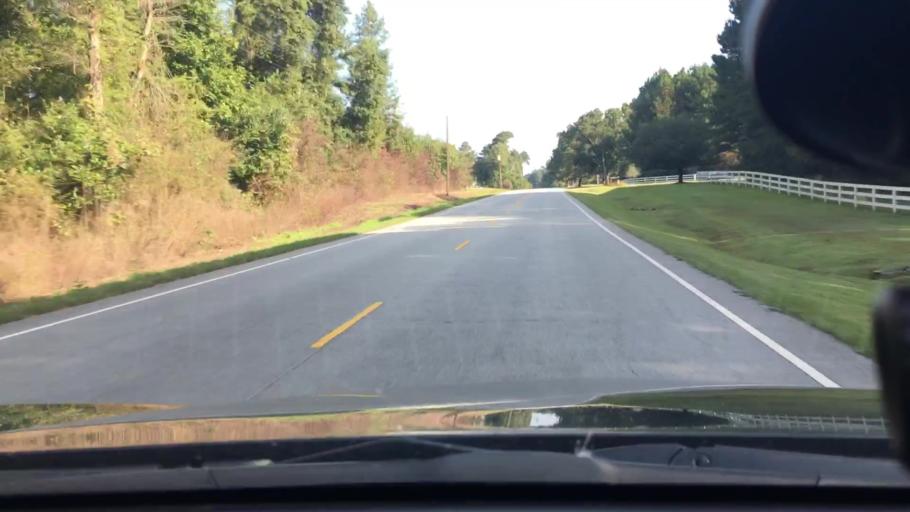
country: US
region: North Carolina
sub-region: Edgecombe County
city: Pinetops
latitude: 35.7249
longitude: -77.5309
